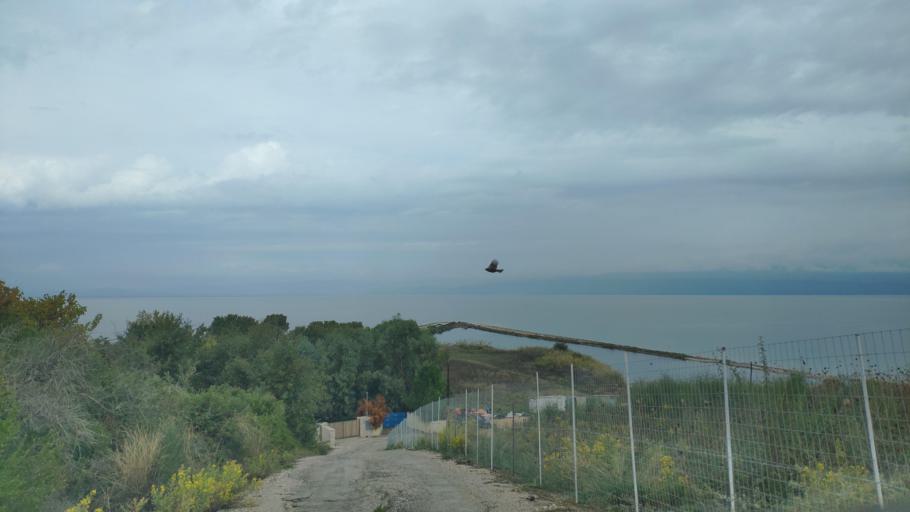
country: GR
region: West Greece
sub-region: Nomos Aitolias kai Akarnanias
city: Monastirakion
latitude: 38.9252
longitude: 21.0222
